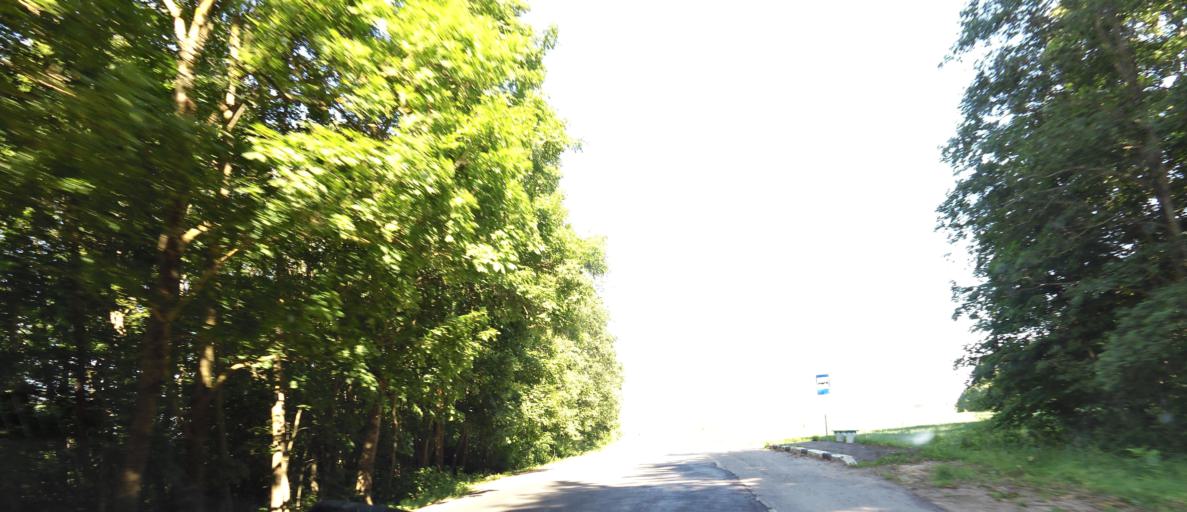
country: LT
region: Panevezys
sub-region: Birzai
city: Birzai
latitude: 56.2095
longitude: 24.6967
